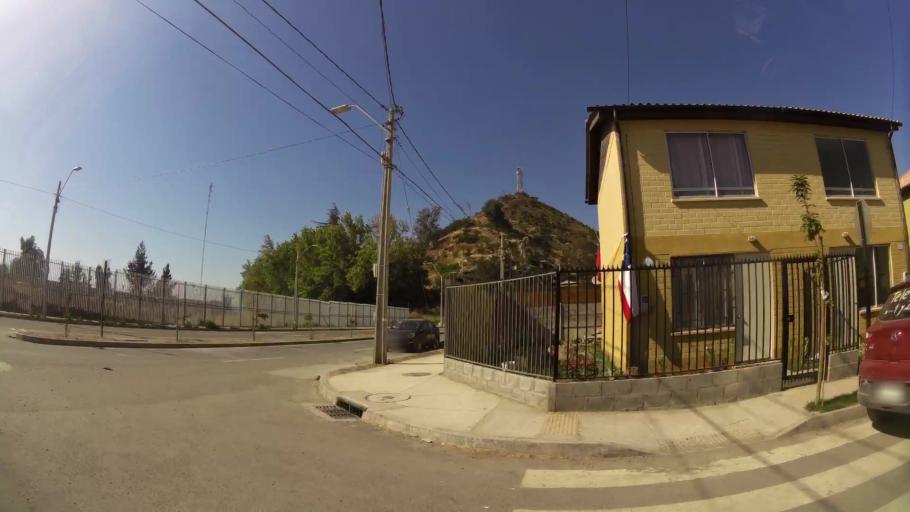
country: CL
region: Santiago Metropolitan
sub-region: Provincia de Maipo
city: San Bernardo
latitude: -33.6107
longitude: -70.6753
